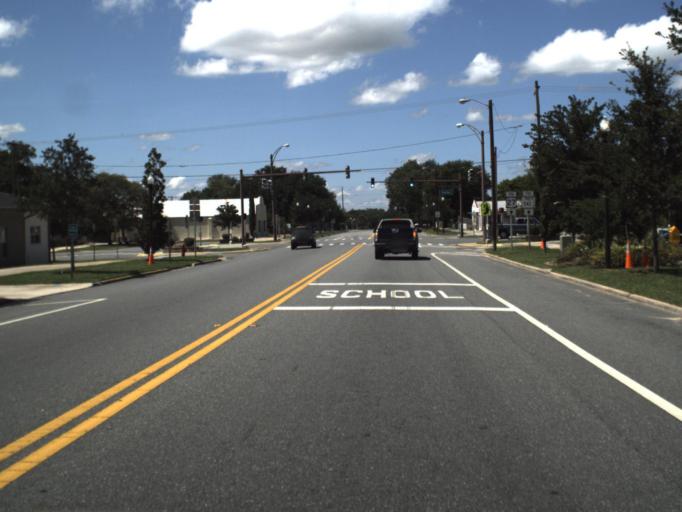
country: US
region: Florida
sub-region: Polk County
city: Dundee
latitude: 28.0224
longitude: -81.6187
